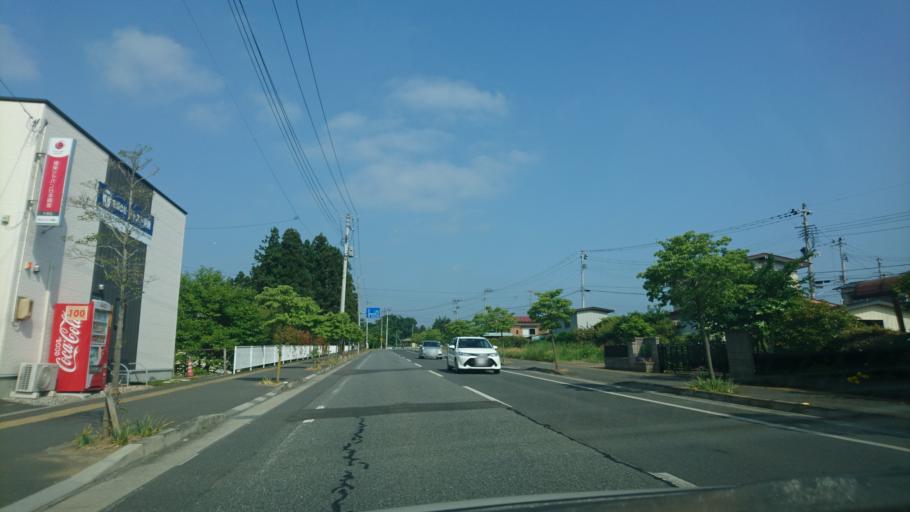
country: JP
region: Iwate
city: Ichinoseki
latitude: 38.9286
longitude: 141.1138
